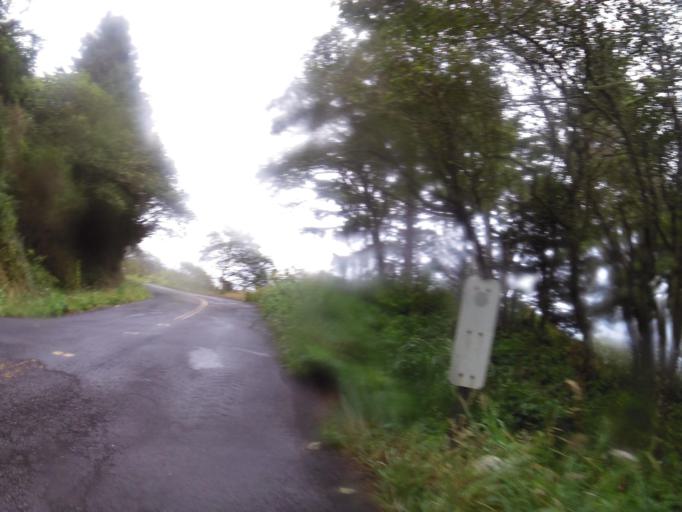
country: US
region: California
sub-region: Humboldt County
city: Westhaven-Moonstone
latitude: 41.1031
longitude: -124.1596
